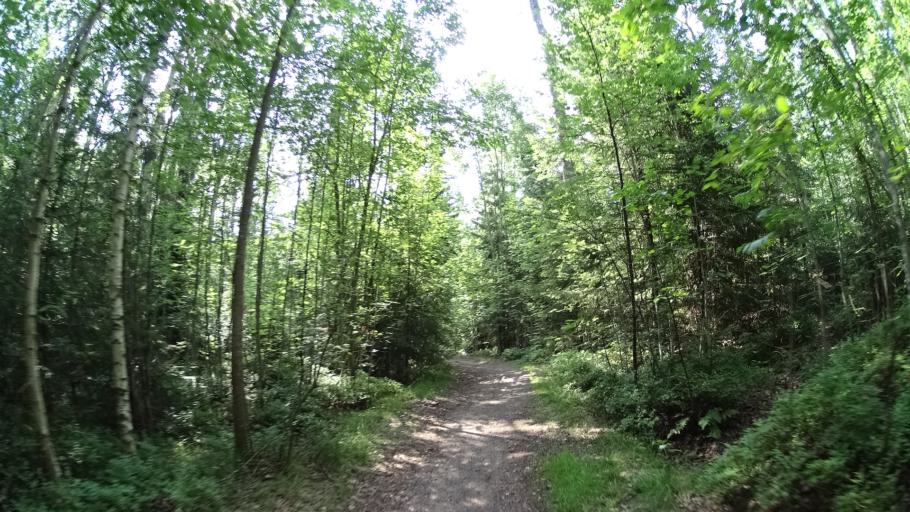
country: FI
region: Uusimaa
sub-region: Helsinki
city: Teekkarikylae
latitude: 60.2736
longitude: 24.9013
